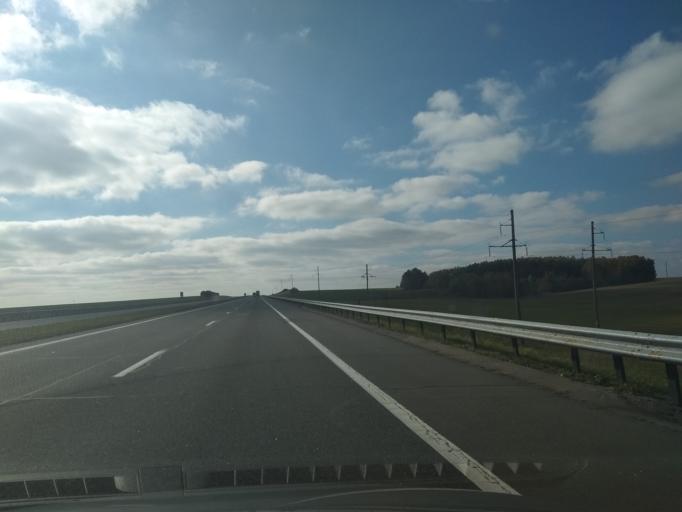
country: BY
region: Minsk
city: Novy Svyerzhan'
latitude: 53.4749
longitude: 26.6224
